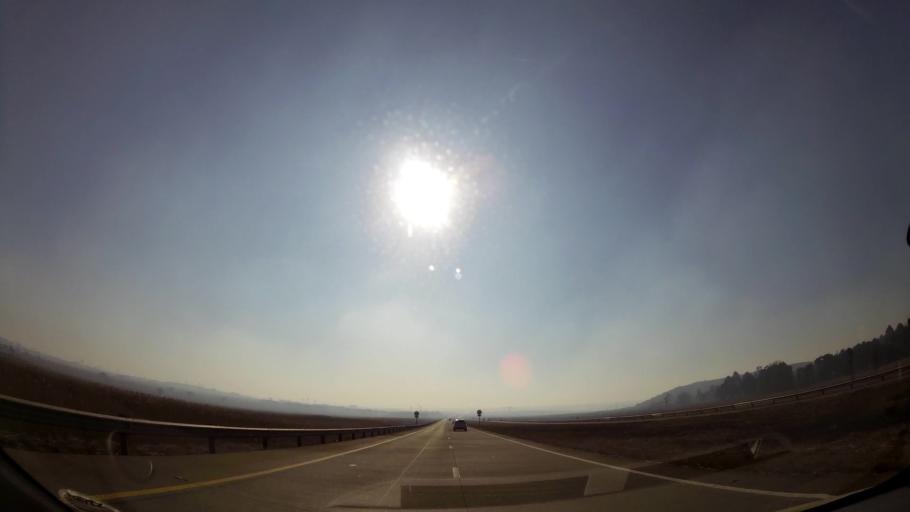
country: ZA
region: Mpumalanga
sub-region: Nkangala District Municipality
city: Witbank
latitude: -25.9421
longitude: 29.2023
